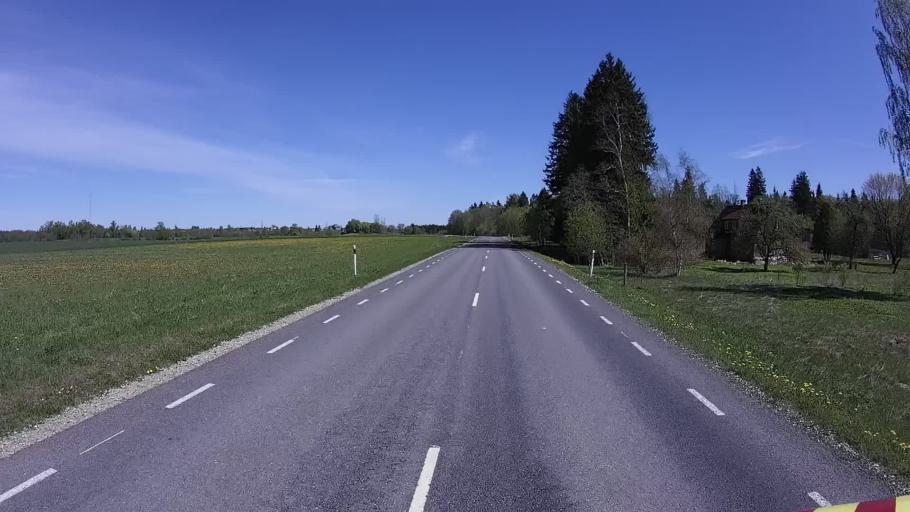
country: EE
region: Raplamaa
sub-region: Kehtna vald
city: Kehtna
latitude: 59.0425
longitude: 25.0984
